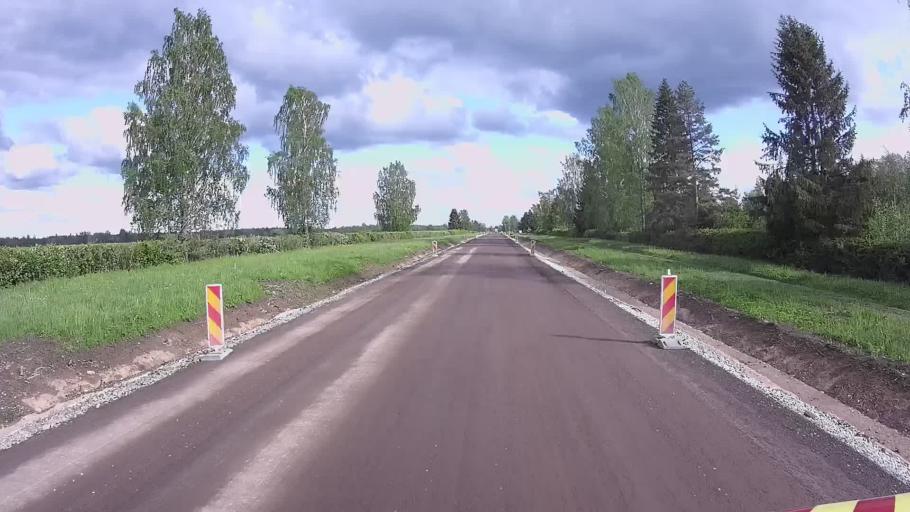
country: EE
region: Jogevamaa
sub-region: Mustvee linn
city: Mustvee
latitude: 59.0240
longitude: 26.6980
